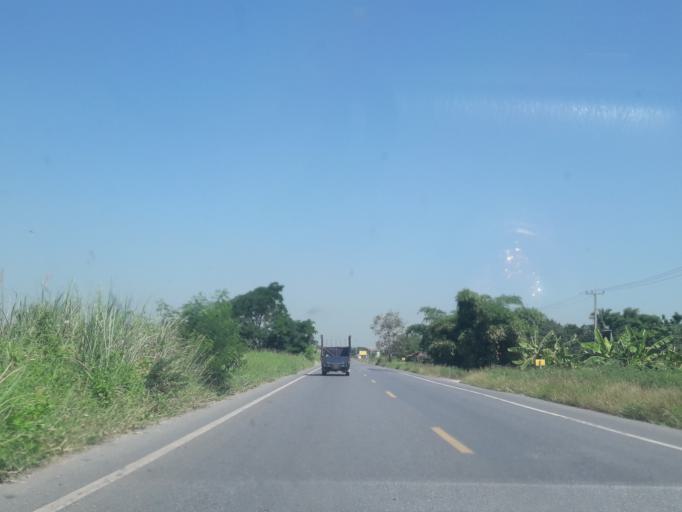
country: TH
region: Sara Buri
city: Nong Khae
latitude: 14.2612
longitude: 100.8233
